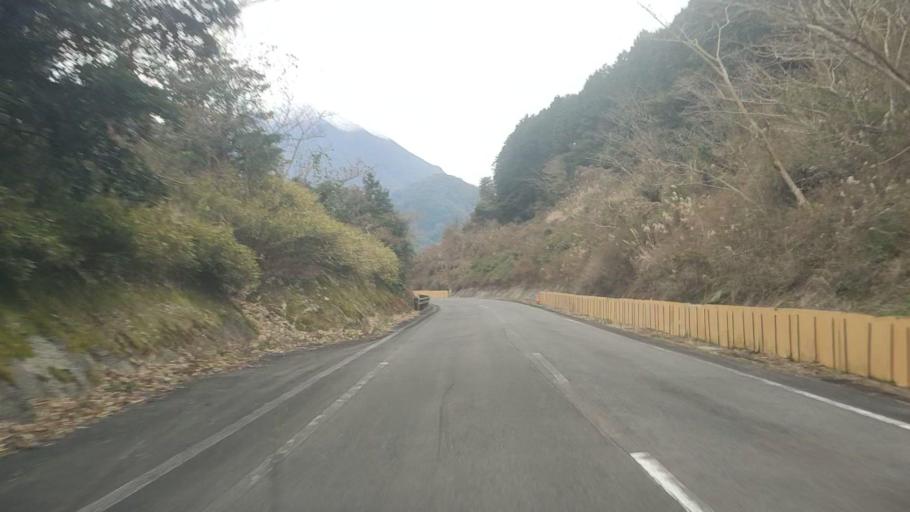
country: JP
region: Nagasaki
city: Shimabara
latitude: 32.7876
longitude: 130.2834
